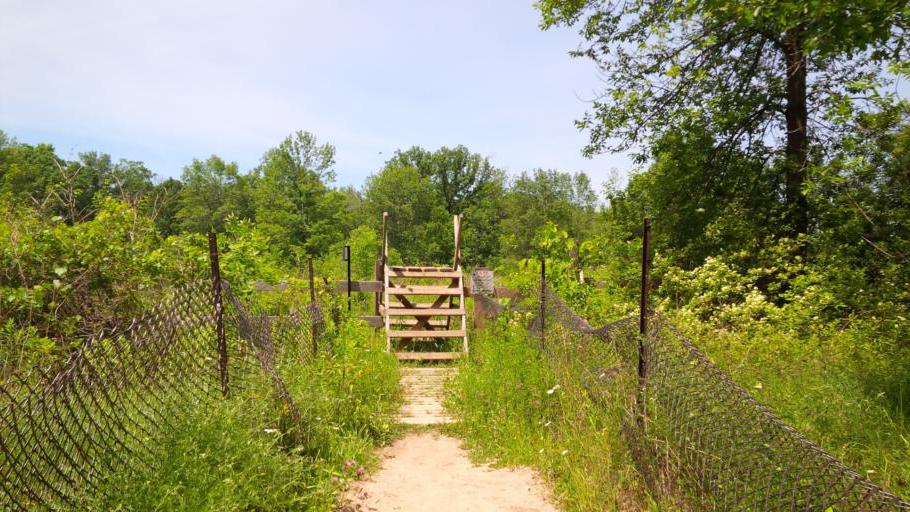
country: CA
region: Ontario
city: Burlington
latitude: 43.3339
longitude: -79.8719
